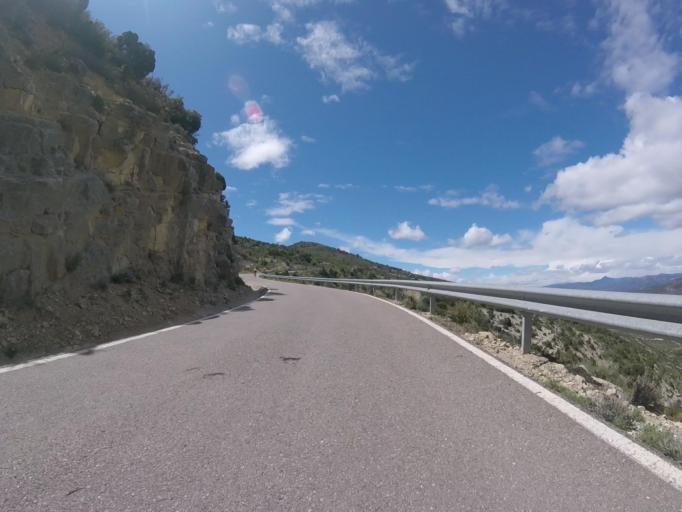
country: ES
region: Valencia
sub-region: Provincia de Castello
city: Sierra-Engarceran
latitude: 40.2820
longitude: -0.0315
